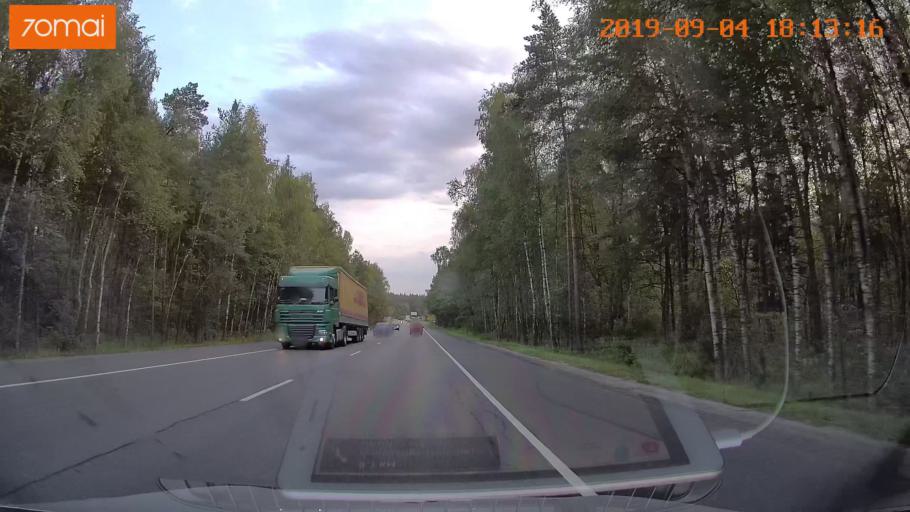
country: RU
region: Moskovskaya
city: Lopatinskiy
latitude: 55.3624
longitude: 38.7352
